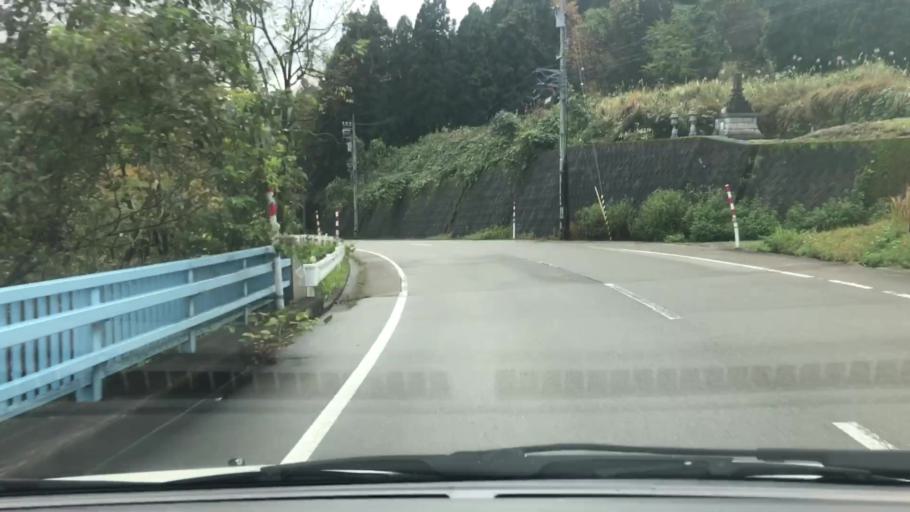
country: JP
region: Toyama
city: Kamiichi
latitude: 36.5929
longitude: 137.3157
